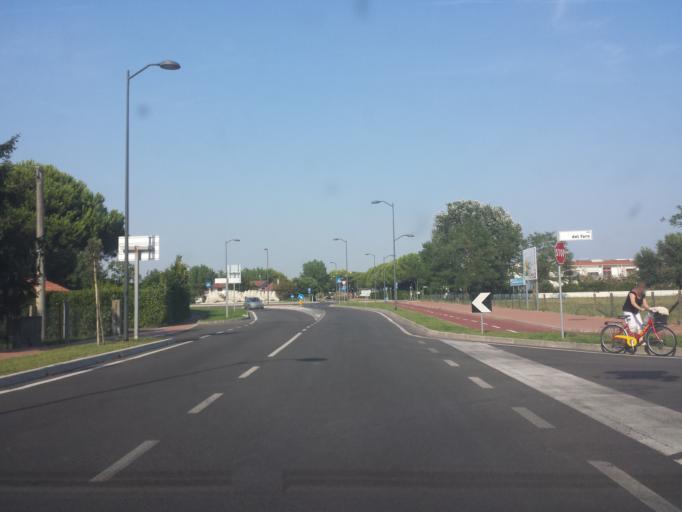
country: IT
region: Veneto
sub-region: Provincia di Venezia
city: Cavallino
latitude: 45.4826
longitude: 12.5777
